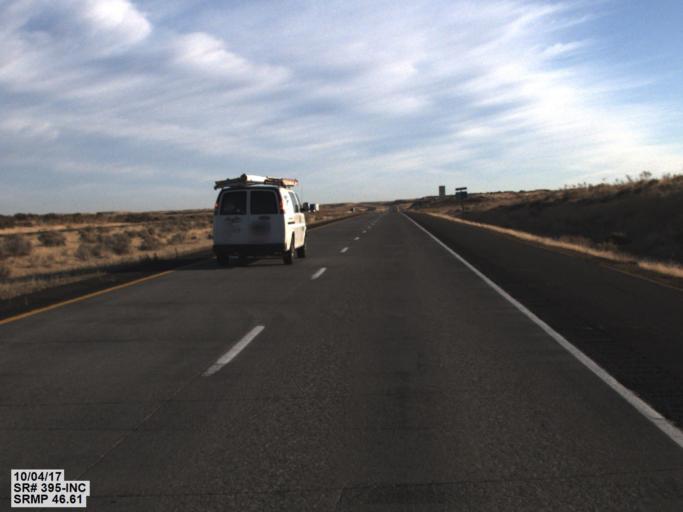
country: US
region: Washington
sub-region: Franklin County
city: Connell
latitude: 46.5747
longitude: -118.9828
